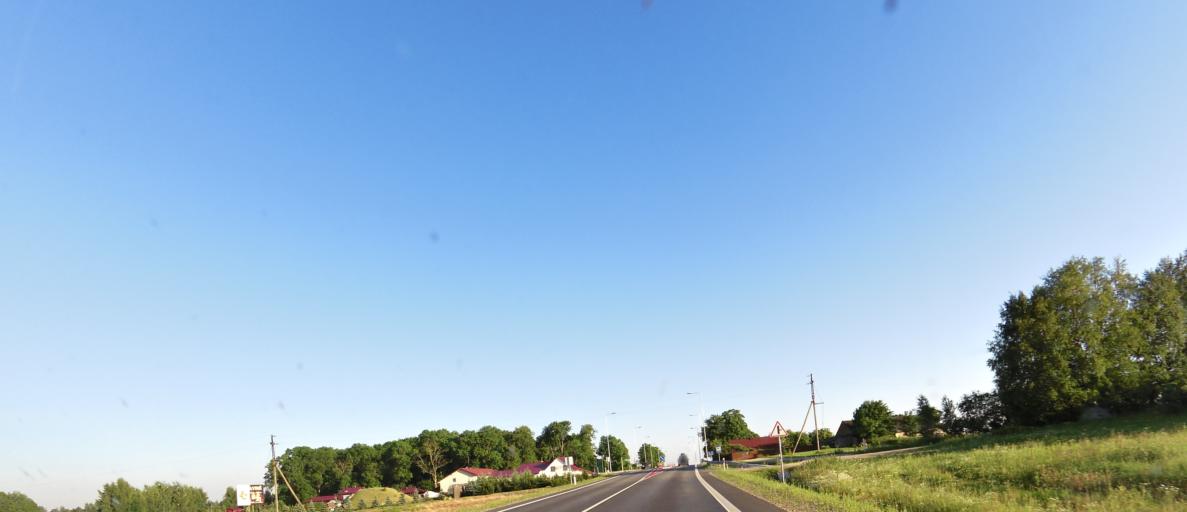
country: LT
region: Panevezys
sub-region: Panevezys City
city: Panevezys
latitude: 55.6223
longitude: 24.3475
